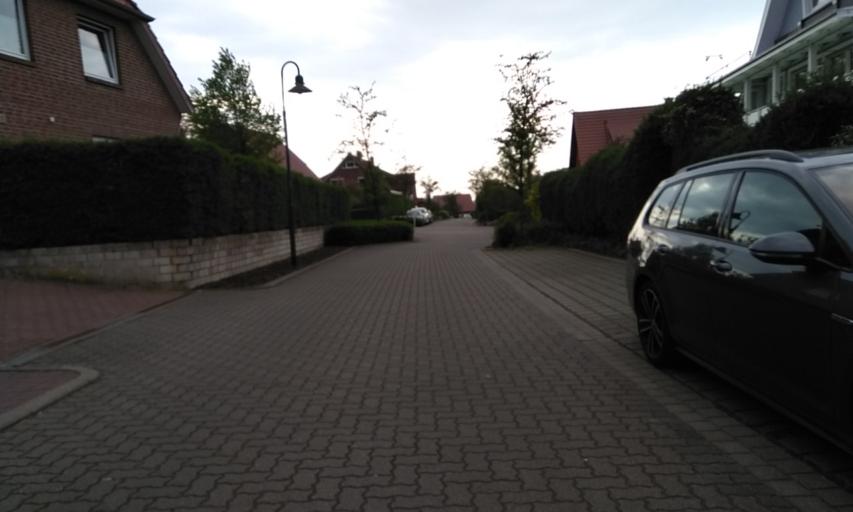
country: DE
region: Lower Saxony
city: Harsefeld
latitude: 53.4579
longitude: 9.5165
